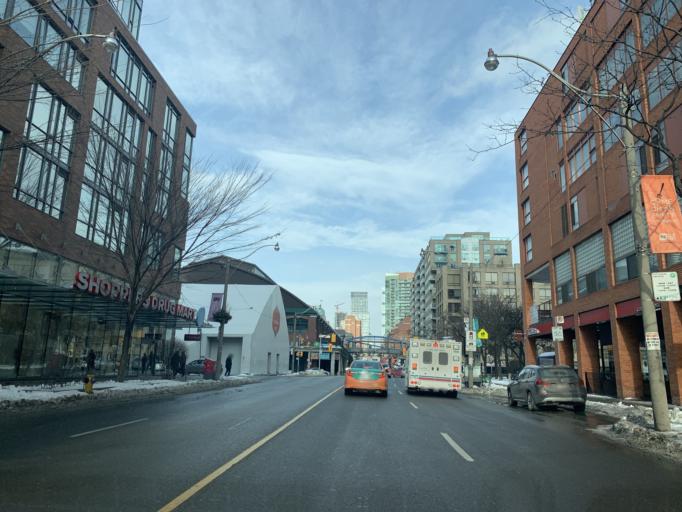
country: CA
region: Ontario
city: Toronto
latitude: 43.6474
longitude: -79.3706
